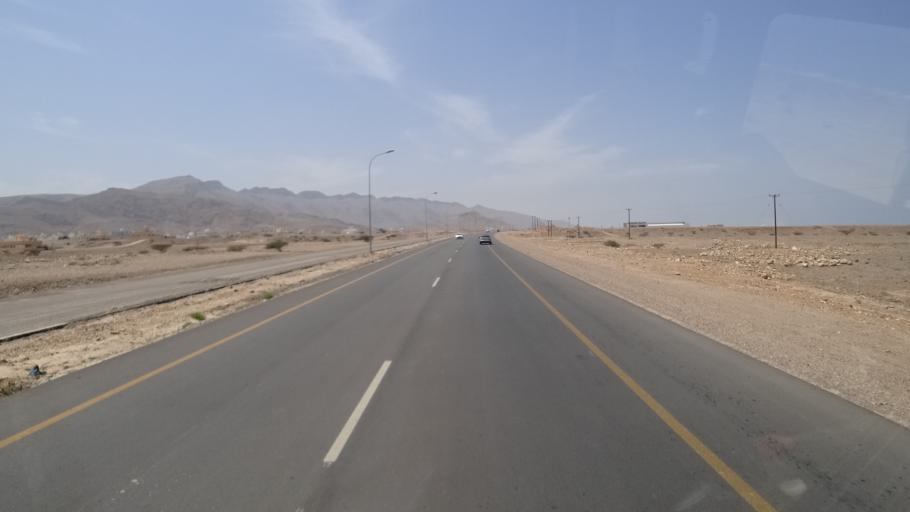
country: OM
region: Ash Sharqiyah
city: Sur
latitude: 22.5870
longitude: 59.4428
